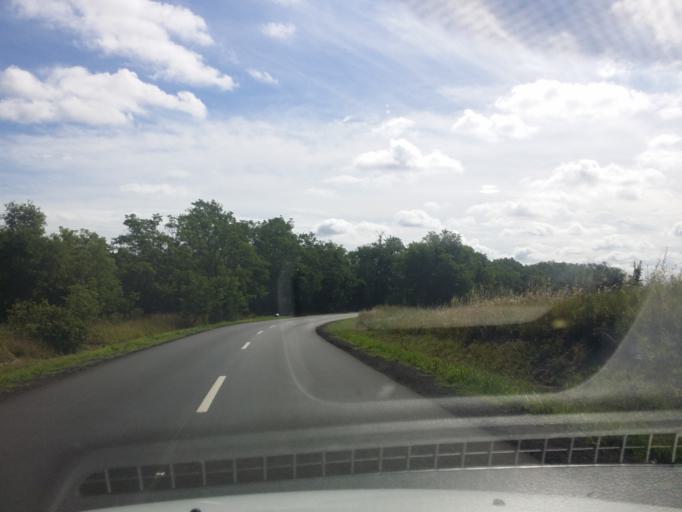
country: HU
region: Heves
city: Heves
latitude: 47.6243
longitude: 20.2457
